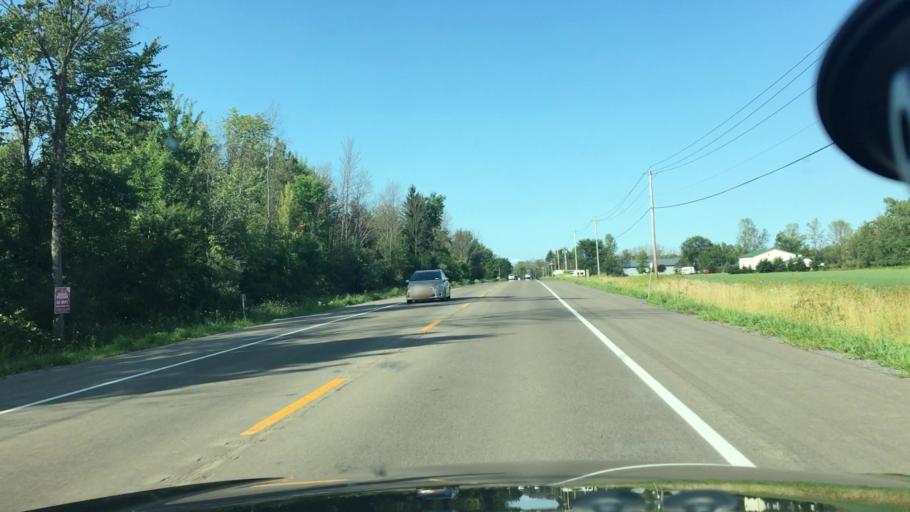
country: US
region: New York
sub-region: Erie County
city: Eden
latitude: 42.6766
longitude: -78.9530
